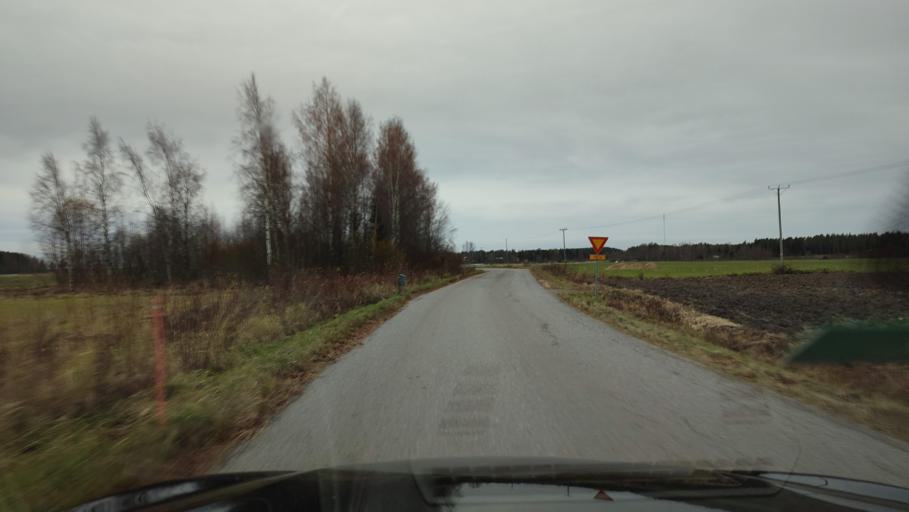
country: FI
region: Ostrobothnia
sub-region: Sydosterbotten
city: Naerpes
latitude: 62.4064
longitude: 21.3930
